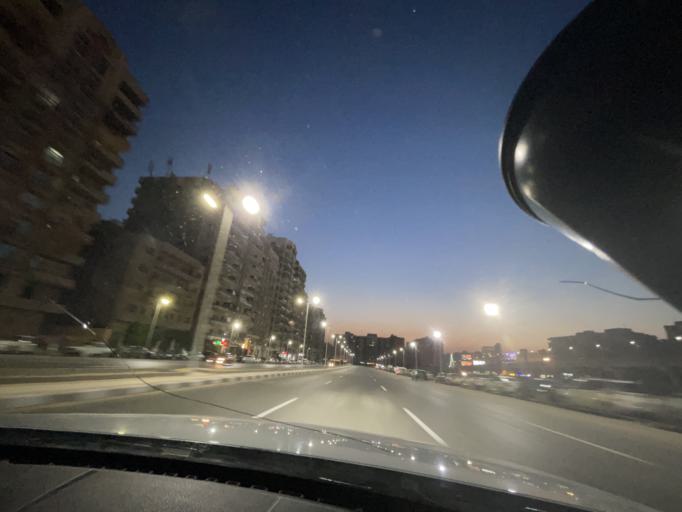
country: EG
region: Muhafazat al Qahirah
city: Cairo
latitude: 30.0691
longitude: 31.3517
